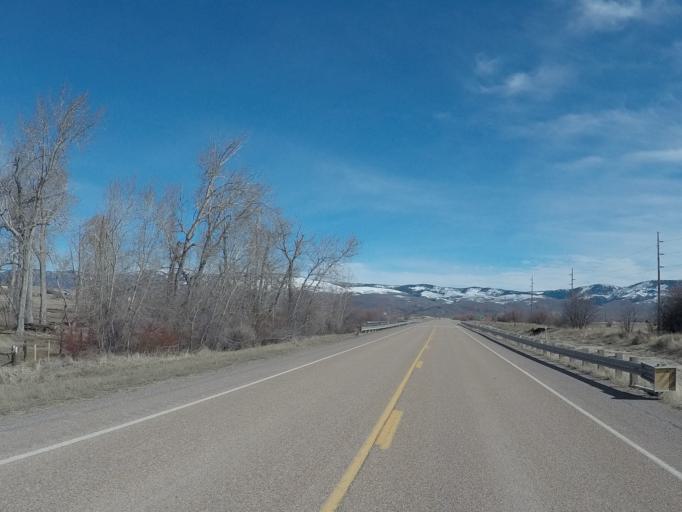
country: US
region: Montana
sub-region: Granite County
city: Philipsburg
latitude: 46.6129
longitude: -113.1784
